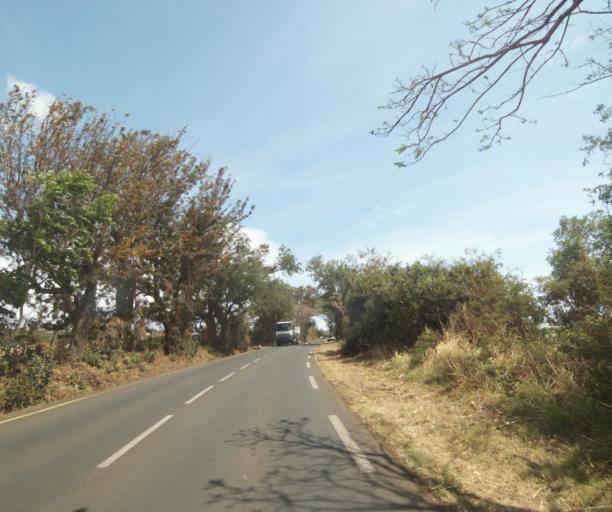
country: RE
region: Reunion
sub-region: Reunion
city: Trois-Bassins
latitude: -21.0666
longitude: 55.2670
